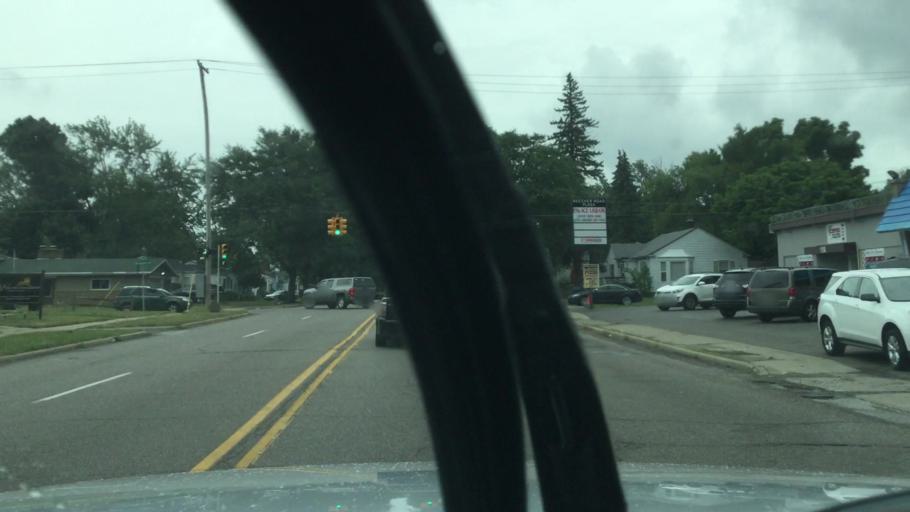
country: US
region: Michigan
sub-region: Genesee County
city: Flint
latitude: 43.0108
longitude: -83.7314
